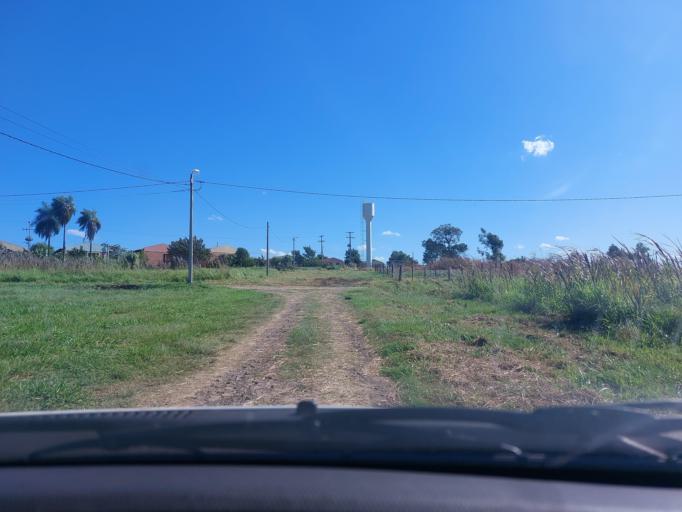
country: PY
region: San Pedro
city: Guayaybi
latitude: -24.6522
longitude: -56.4509
